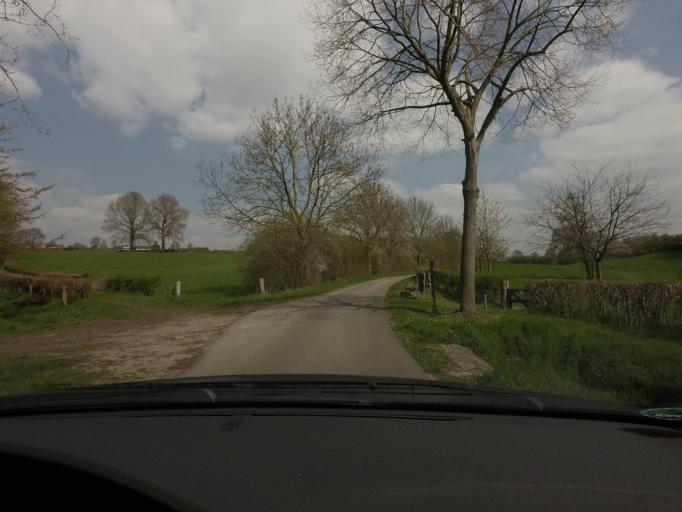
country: NL
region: Limburg
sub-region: Eijsden-Margraten
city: Margraten
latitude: 50.7837
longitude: 5.8069
